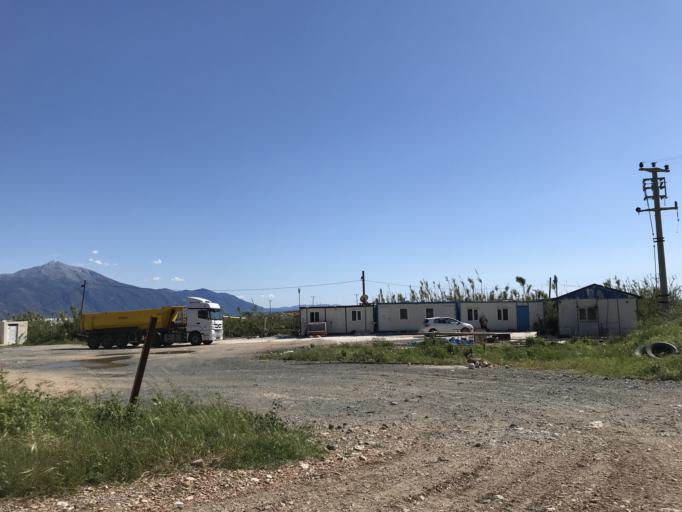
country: TR
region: Hatay
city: Samandag
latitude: 36.1140
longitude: 35.9288
